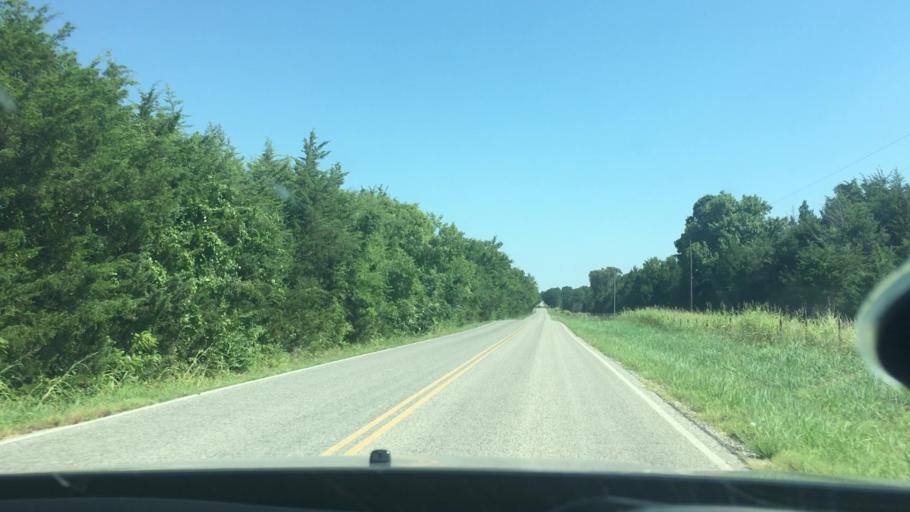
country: US
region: Oklahoma
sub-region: Johnston County
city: Tishomingo
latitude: 34.2817
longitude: -96.6185
